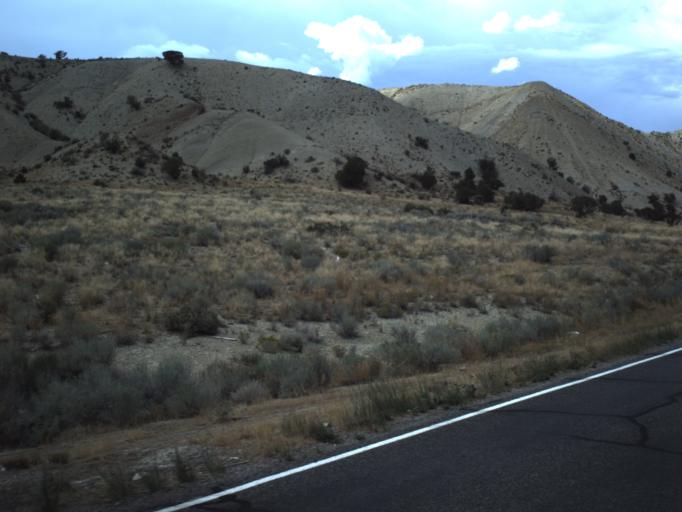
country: US
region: Utah
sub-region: Sanpete County
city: Centerfield
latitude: 39.1345
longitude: -111.7291
